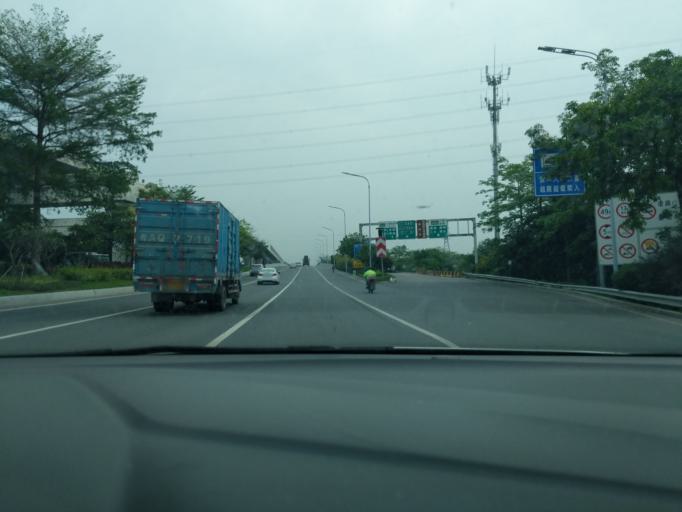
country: CN
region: Guangdong
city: Huangge
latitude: 22.8563
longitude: 113.4890
